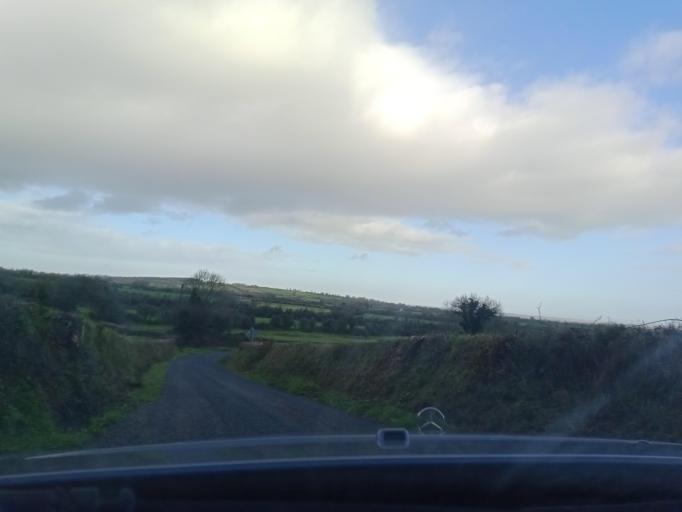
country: IE
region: Leinster
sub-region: Kilkenny
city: Callan
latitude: 52.4671
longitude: -7.3946
